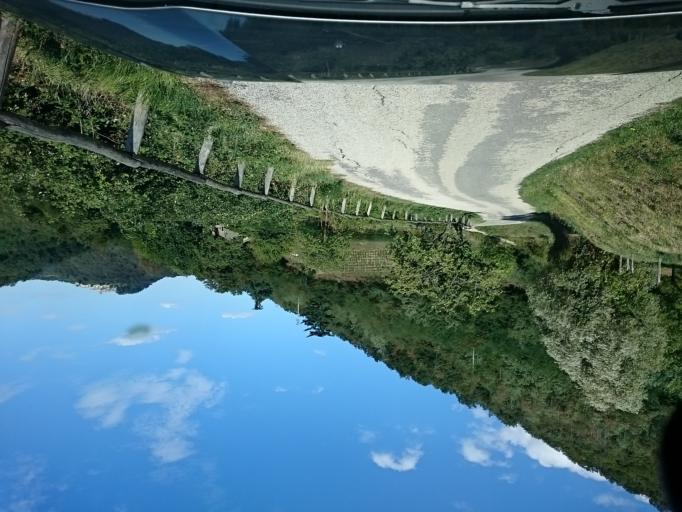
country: IT
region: Veneto
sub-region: Provincia di Padova
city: Galzignano
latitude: 45.3100
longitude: 11.6955
